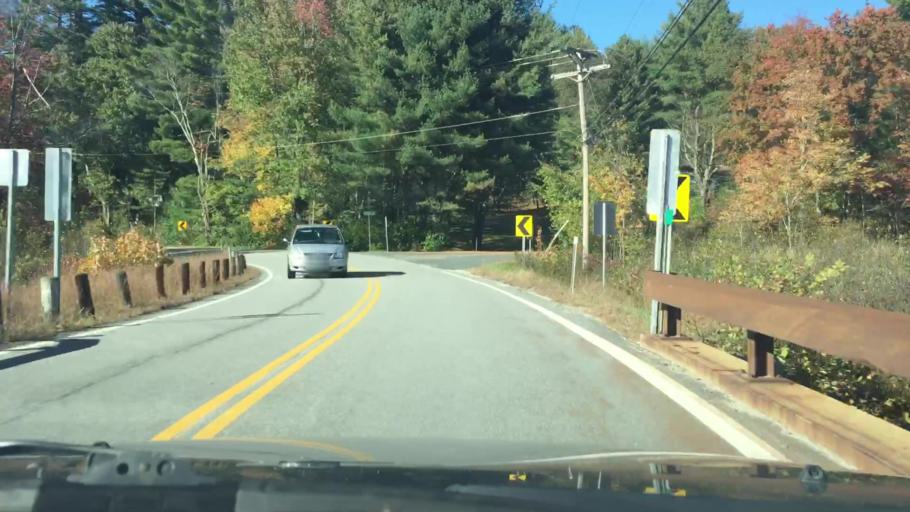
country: US
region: New Hampshire
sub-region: Cheshire County
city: Swanzey
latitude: 42.8358
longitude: -72.2727
